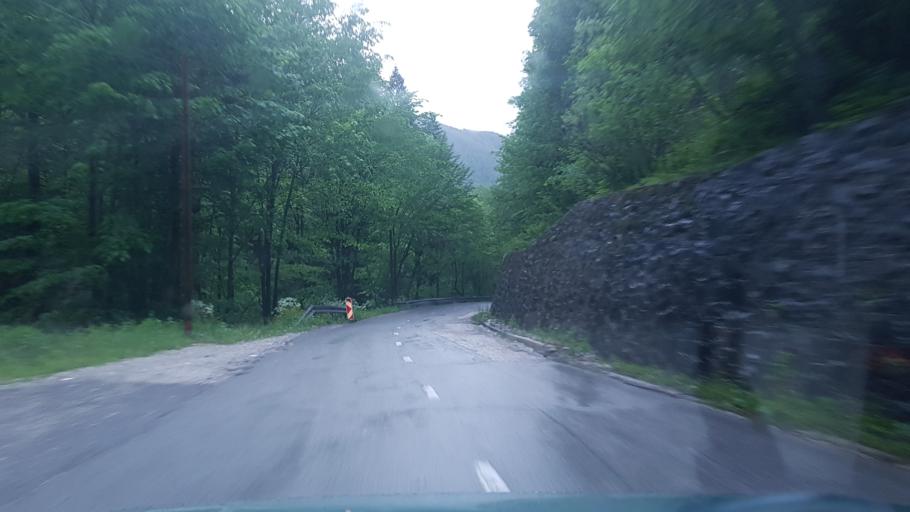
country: SI
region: Bohinj
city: Bohinjska Bistrica
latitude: 46.2137
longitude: 13.9904
